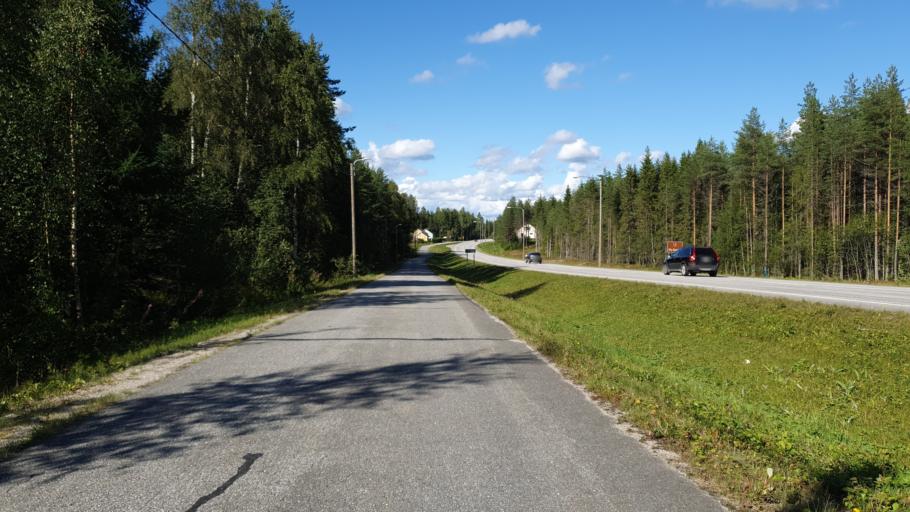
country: FI
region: Kainuu
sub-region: Kehys-Kainuu
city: Kuhmo
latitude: 64.1025
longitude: 29.4757
